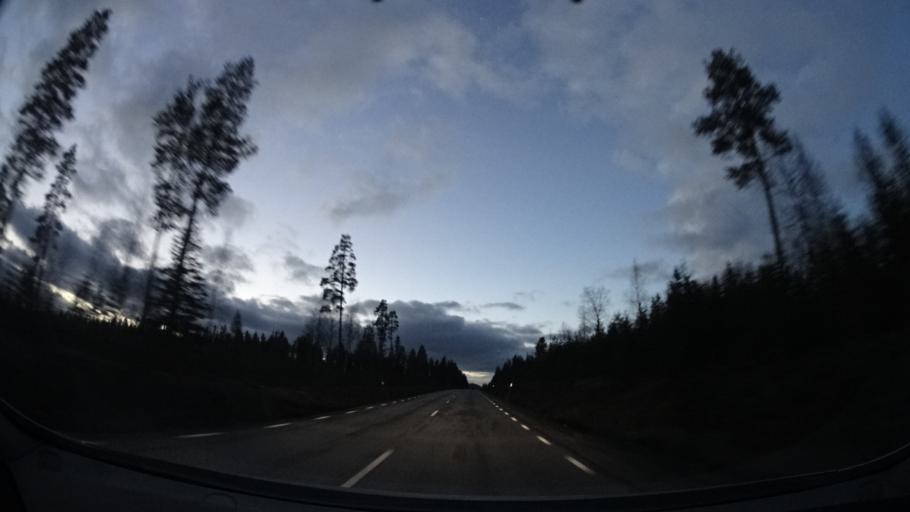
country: SE
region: Vaesterbotten
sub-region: Dorotea Kommun
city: Dorotea
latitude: 64.2226
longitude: 16.8601
